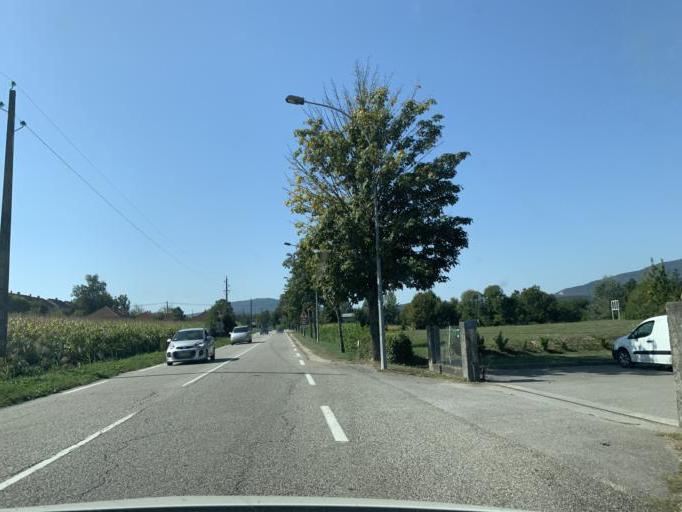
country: FR
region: Rhone-Alpes
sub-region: Departement de l'Ain
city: Belley
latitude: 45.7416
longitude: 5.6783
